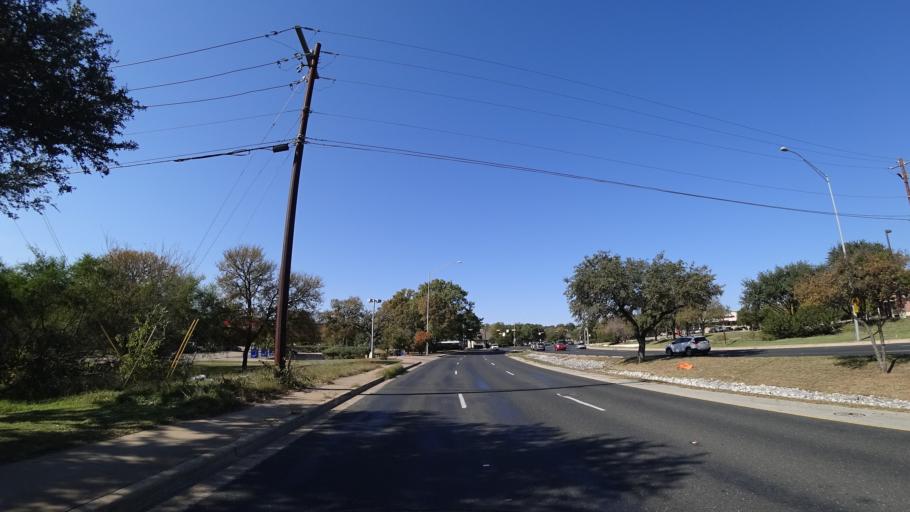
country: US
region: Texas
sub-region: Travis County
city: Barton Creek
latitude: 30.2292
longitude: -97.8638
